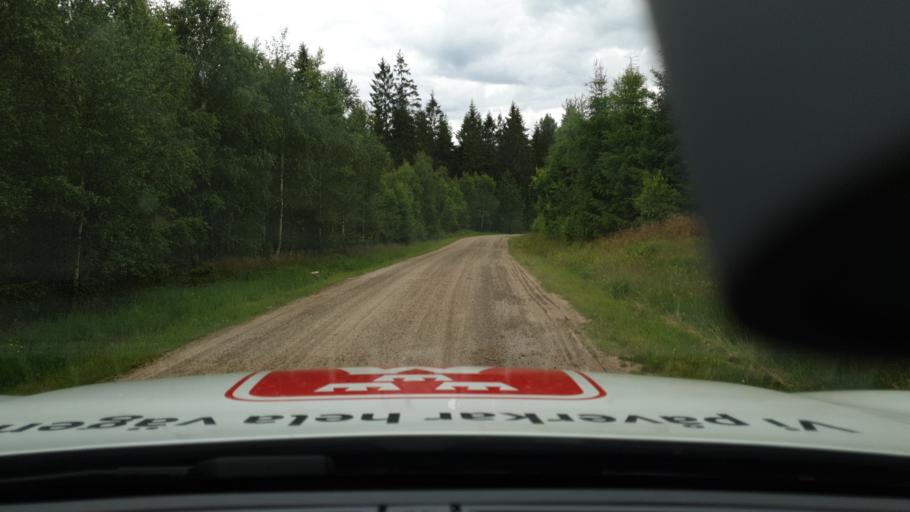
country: SE
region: Joenkoeping
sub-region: Varnamo Kommun
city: Forsheda
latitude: 57.1345
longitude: 13.9240
